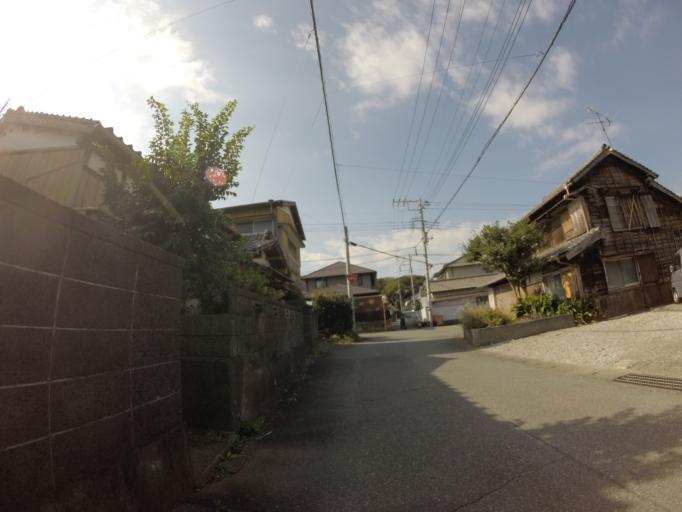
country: JP
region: Shizuoka
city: Fuji
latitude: 35.1284
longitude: 138.6702
